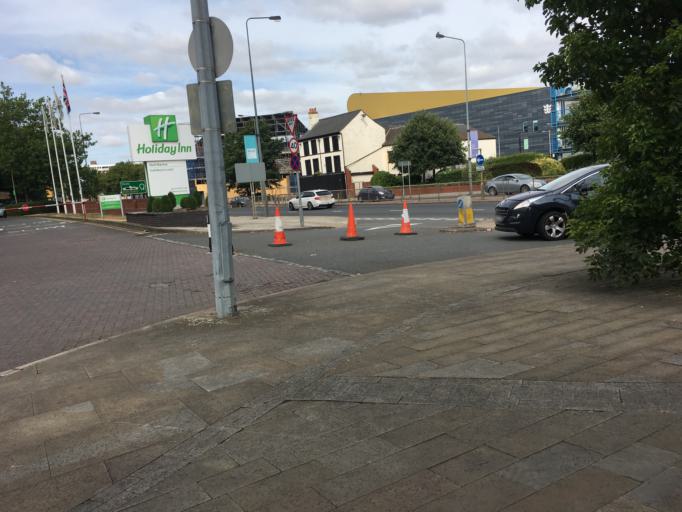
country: GB
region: England
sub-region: City of Kingston upon Hull
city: Hull
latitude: 53.7408
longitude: -0.3398
